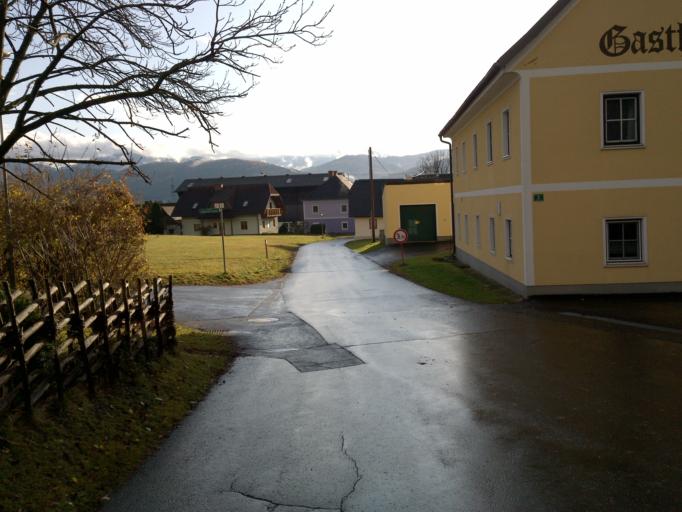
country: AT
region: Styria
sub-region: Politischer Bezirk Murtal
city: Kobenz
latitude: 47.2373
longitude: 14.8335
